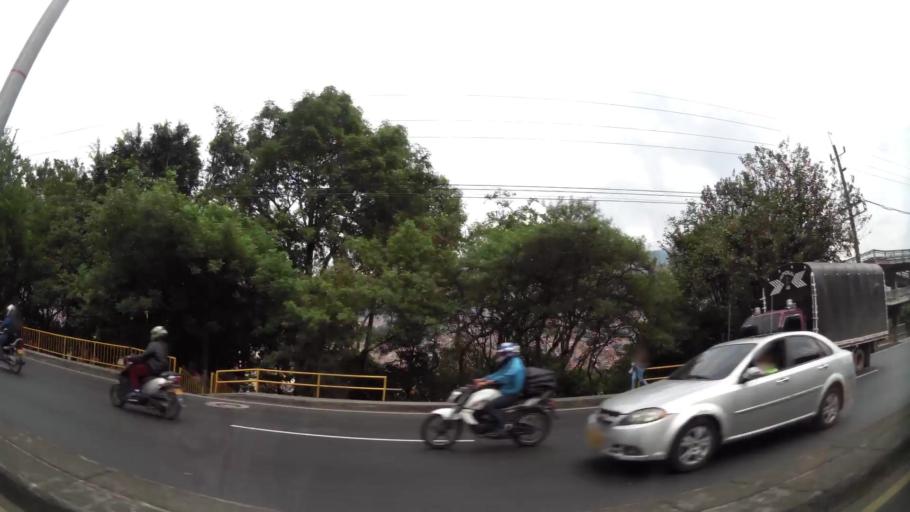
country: CO
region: Antioquia
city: Bello
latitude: 6.3054
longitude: -75.5604
